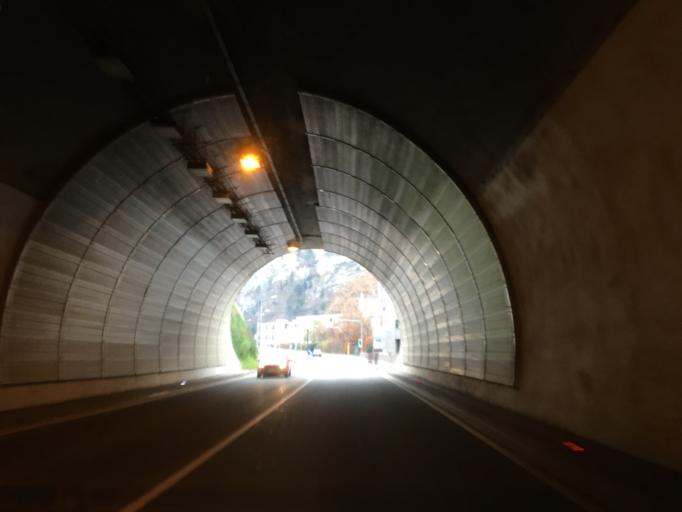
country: AT
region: Vorarlberg
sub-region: Politischer Bezirk Feldkirch
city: Feldkirch
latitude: 47.2365
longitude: 9.5996
